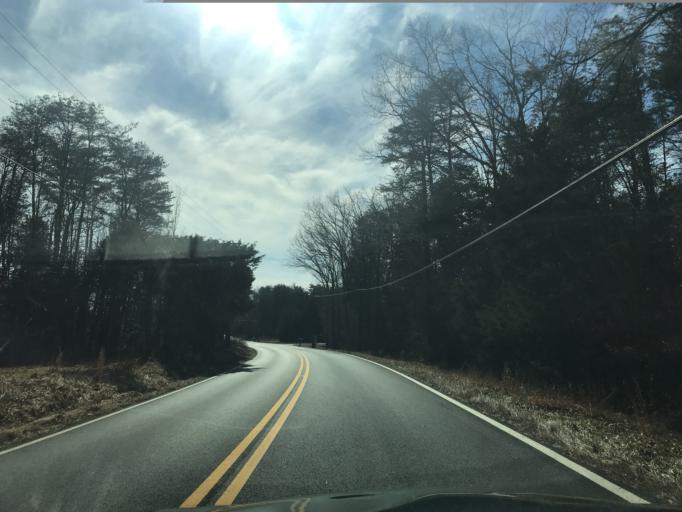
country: US
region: Maryland
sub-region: Charles County
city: Indian Head
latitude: 38.5232
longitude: -77.1459
